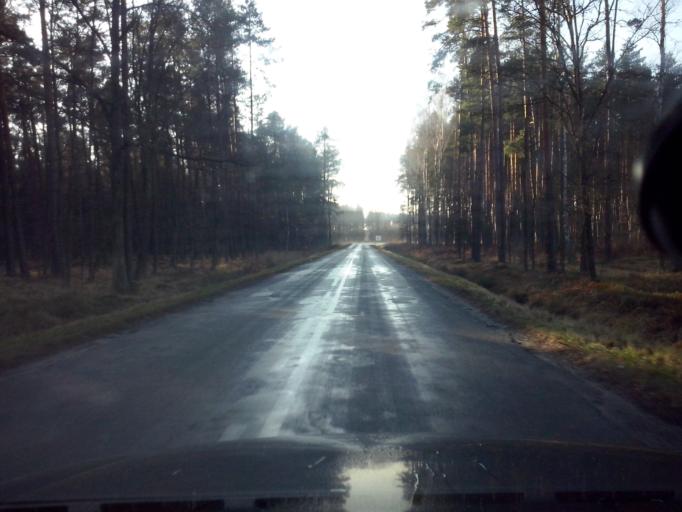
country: PL
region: Subcarpathian Voivodeship
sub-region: Powiat lezajski
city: Letownia
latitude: 50.3667
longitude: 22.2466
